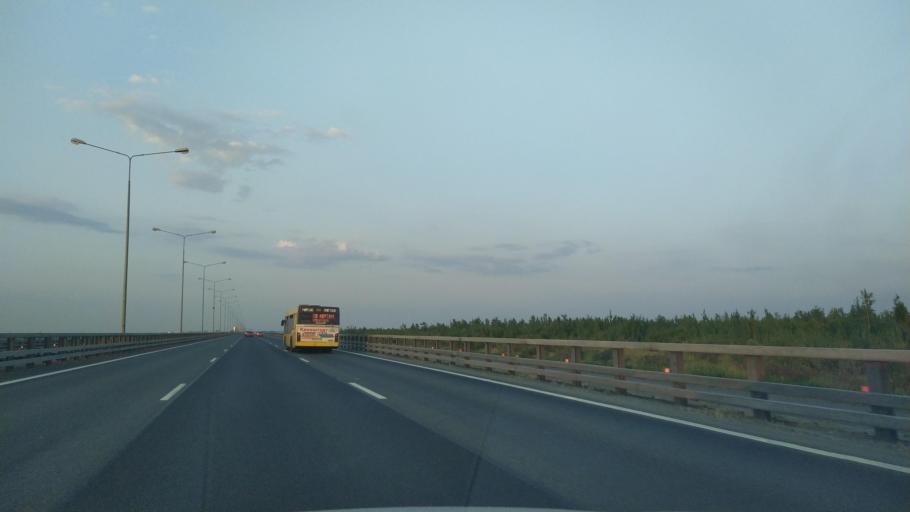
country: RU
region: St.-Petersburg
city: Kronshtadt
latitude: 60.0214
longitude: 29.7490
